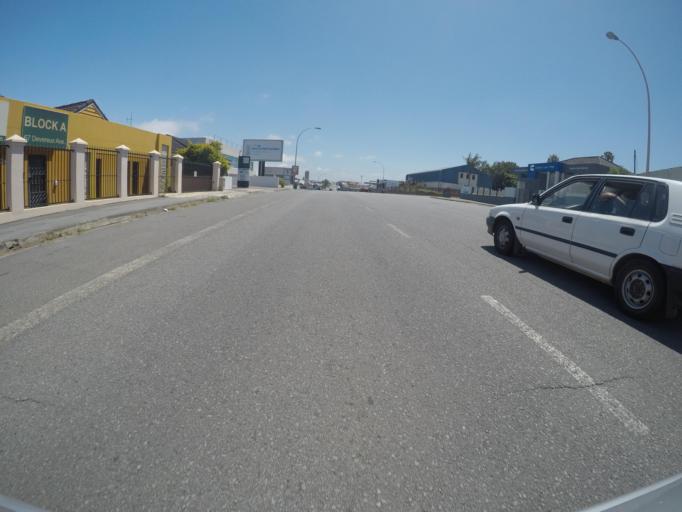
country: ZA
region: Eastern Cape
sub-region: Buffalo City Metropolitan Municipality
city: East London
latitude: -32.9847
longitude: 27.9084
